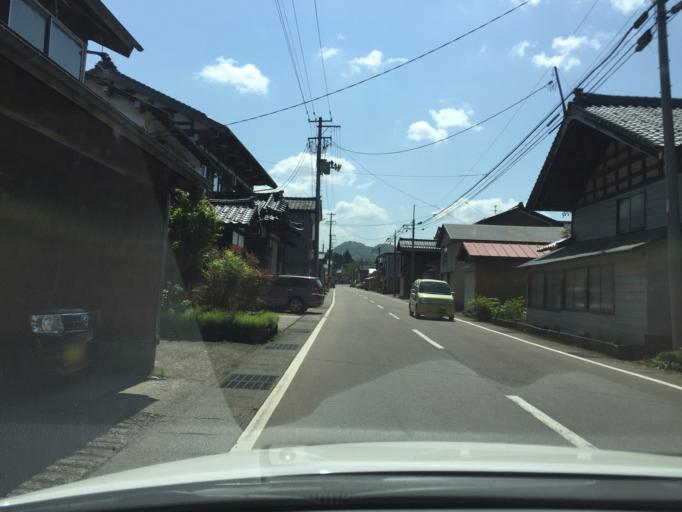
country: JP
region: Niigata
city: Tochio-honcho
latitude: 37.5482
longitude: 139.0873
